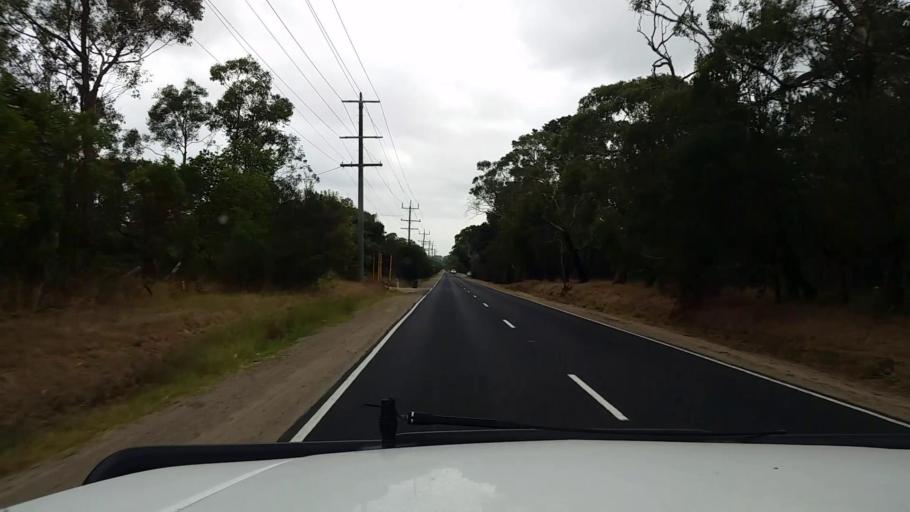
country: AU
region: Victoria
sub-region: Mornington Peninsula
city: Somerville
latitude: -38.2113
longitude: 145.1572
